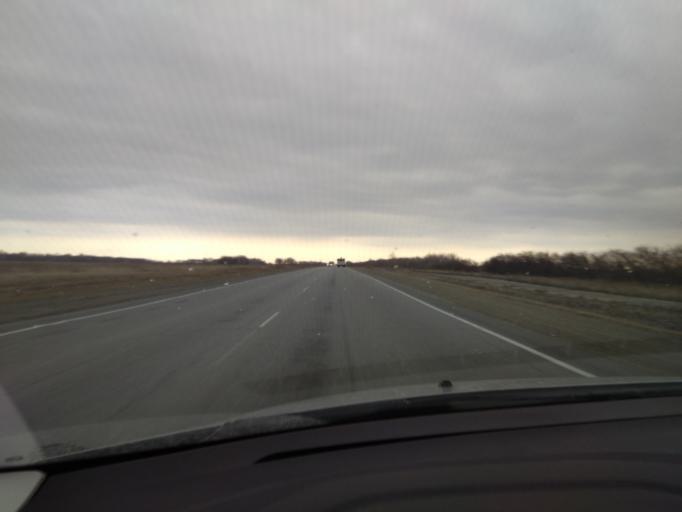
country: RU
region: Chelyabinsk
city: Tyubuk
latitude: 55.8397
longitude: 61.1774
